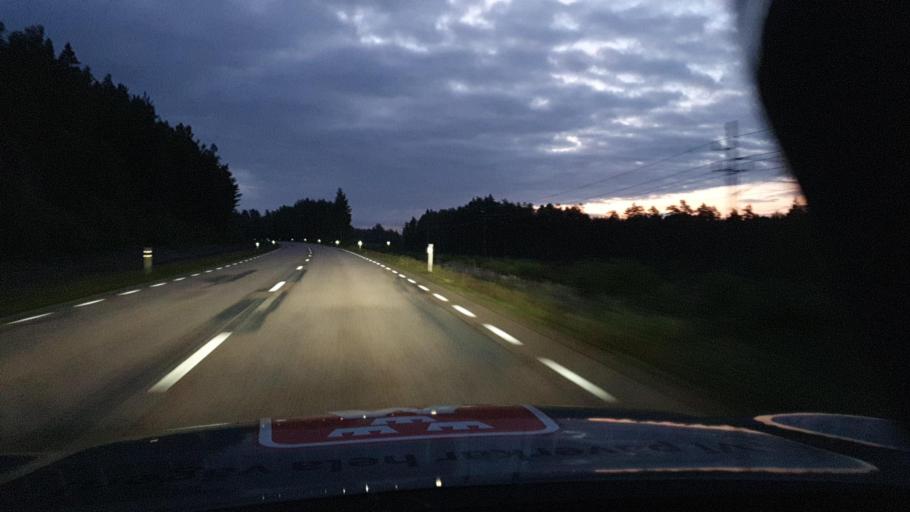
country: SE
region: Vaermland
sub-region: Storfors Kommun
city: Storfors
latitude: 59.4046
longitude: 14.2177
